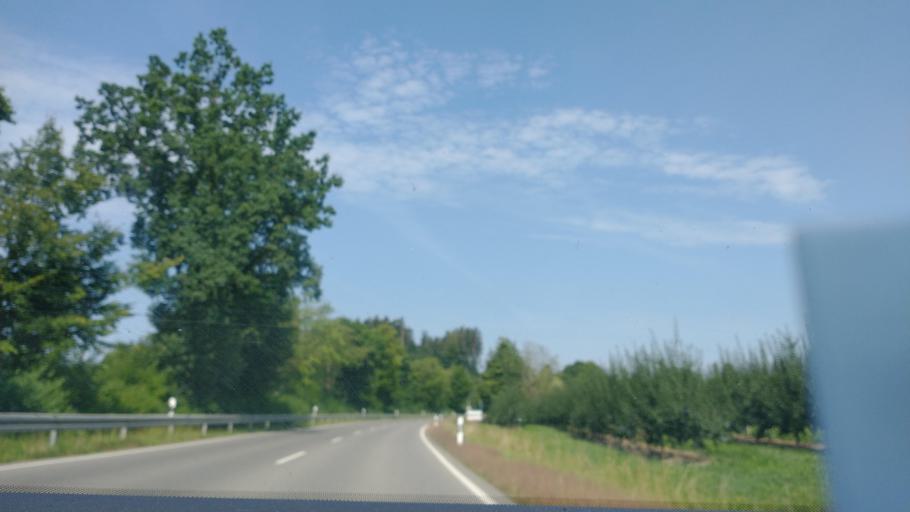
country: DE
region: Baden-Wuerttemberg
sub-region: Tuebingen Region
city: Tettnang
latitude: 47.6650
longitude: 9.6218
